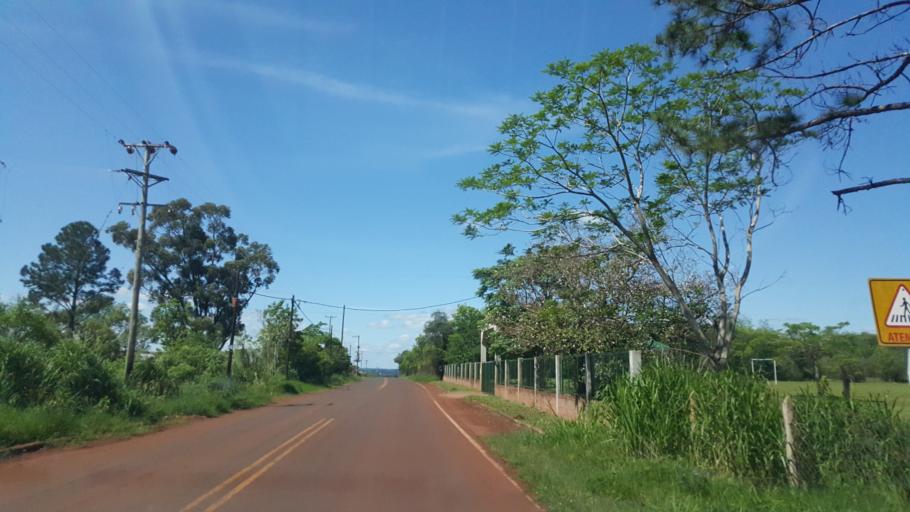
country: AR
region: Misiones
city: Garupa
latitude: -27.5016
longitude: -55.8492
